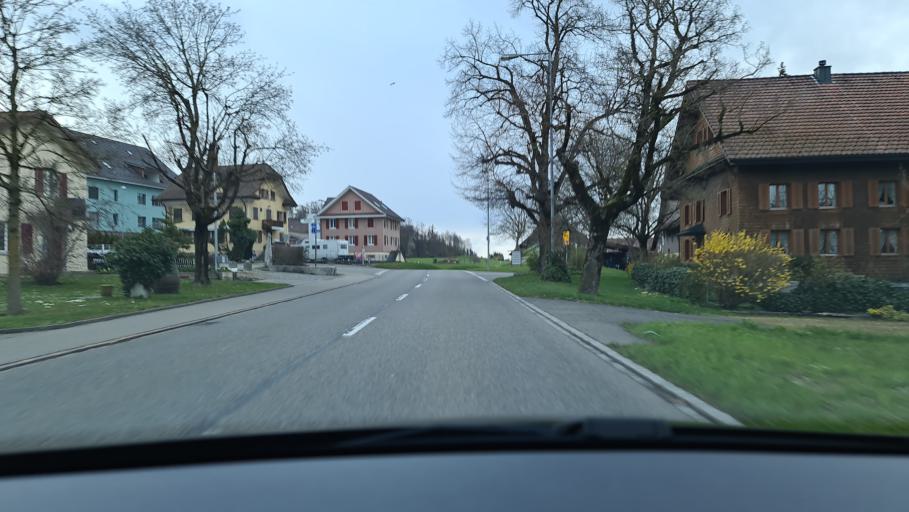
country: CH
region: Aargau
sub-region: Bezirk Muri
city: Auw
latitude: 47.2268
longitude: 8.3664
